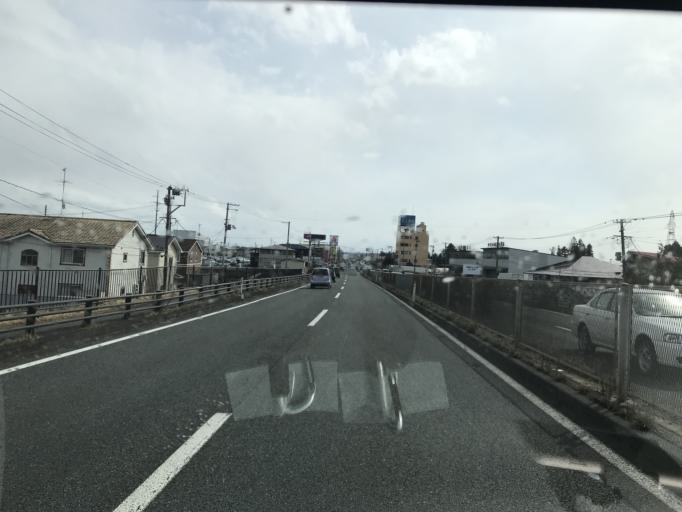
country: JP
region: Iwate
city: Kitakami
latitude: 39.3048
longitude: 141.1088
